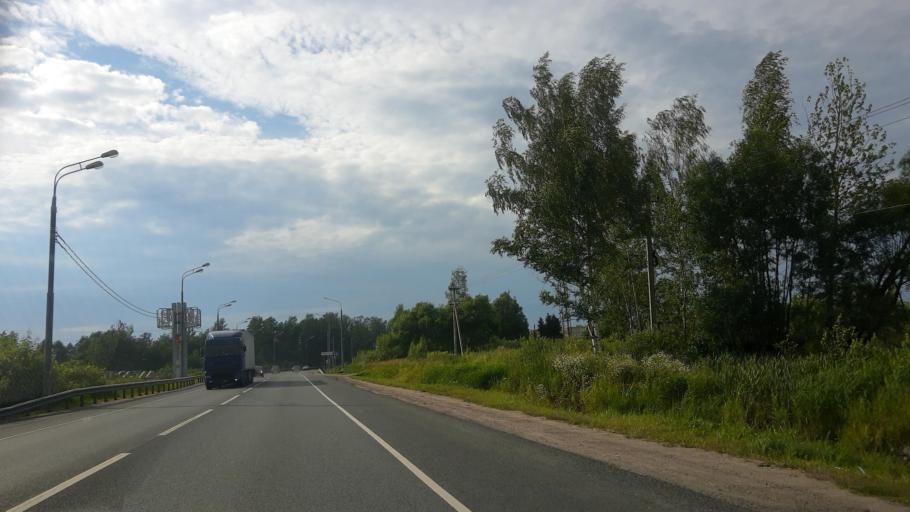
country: RU
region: Moskovskaya
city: Fryazevo
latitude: 55.7521
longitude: 38.4456
